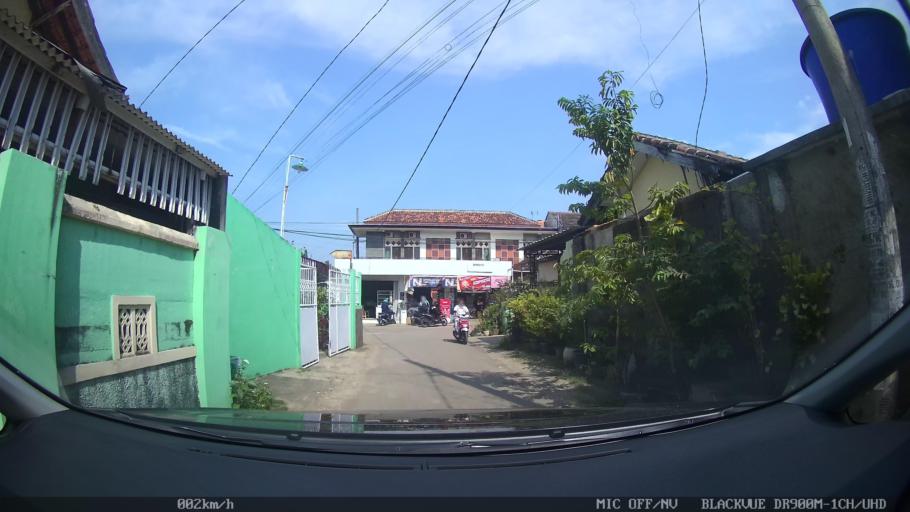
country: ID
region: Lampung
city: Kedaton
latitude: -5.3755
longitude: 105.2380
